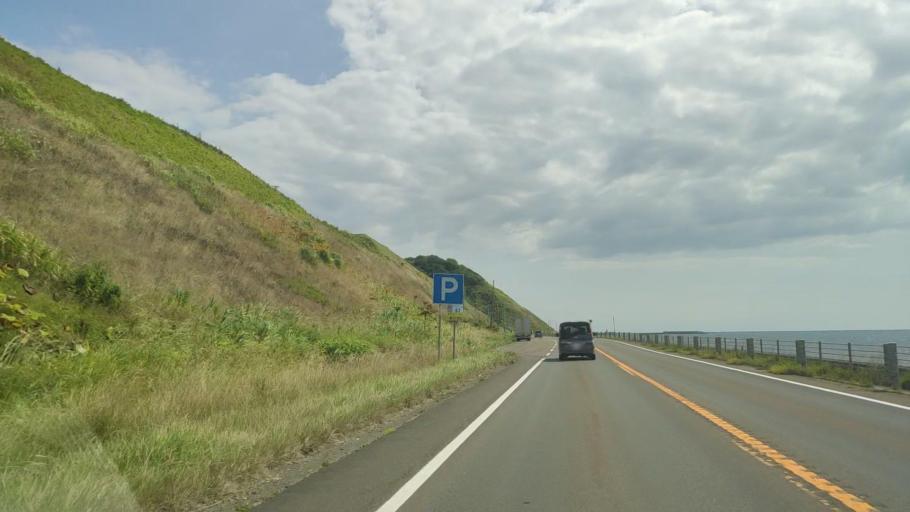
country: JP
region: Hokkaido
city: Rumoi
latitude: 44.2376
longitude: 141.6573
